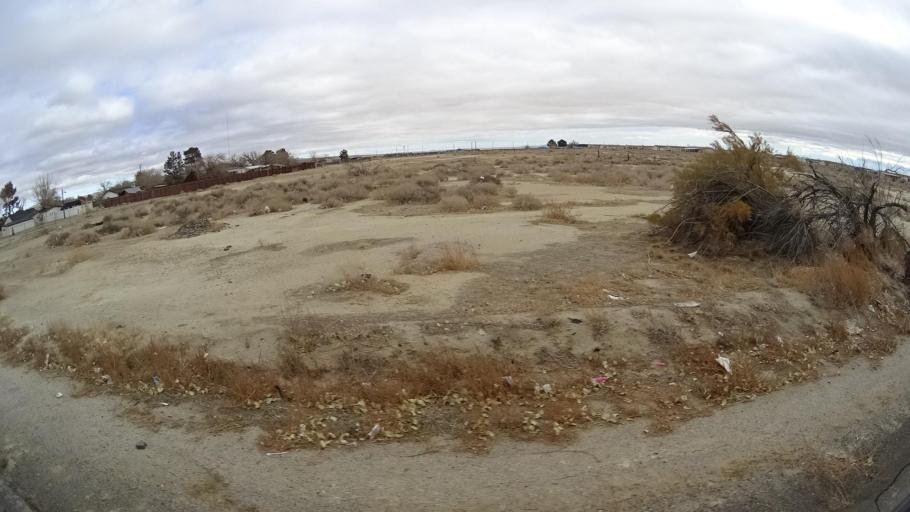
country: US
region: California
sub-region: Kern County
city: Rosamond
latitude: 34.8463
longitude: -118.1670
